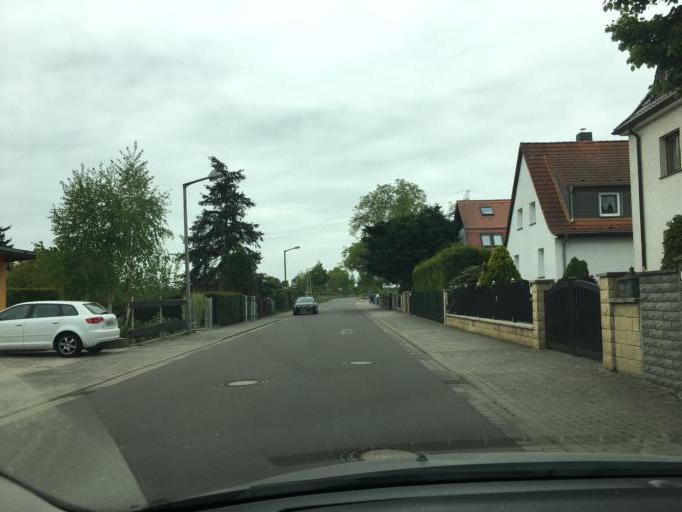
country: DE
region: Saxony
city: Taucha
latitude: 51.3919
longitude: 12.4457
